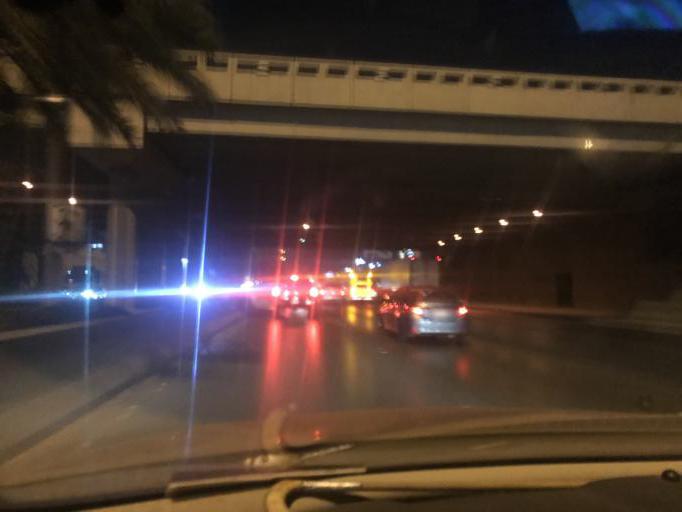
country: SA
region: Ar Riyad
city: Riyadh
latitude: 24.6943
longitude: 46.7737
